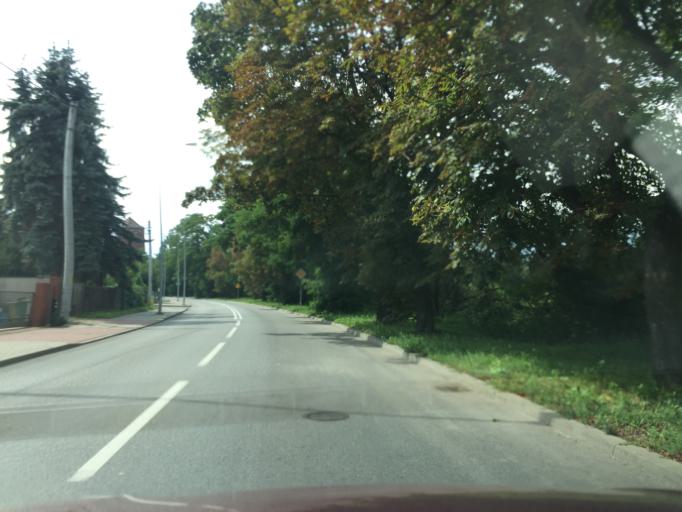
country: PL
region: Greater Poland Voivodeship
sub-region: Kalisz
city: Kalisz
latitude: 51.7439
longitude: 18.0770
